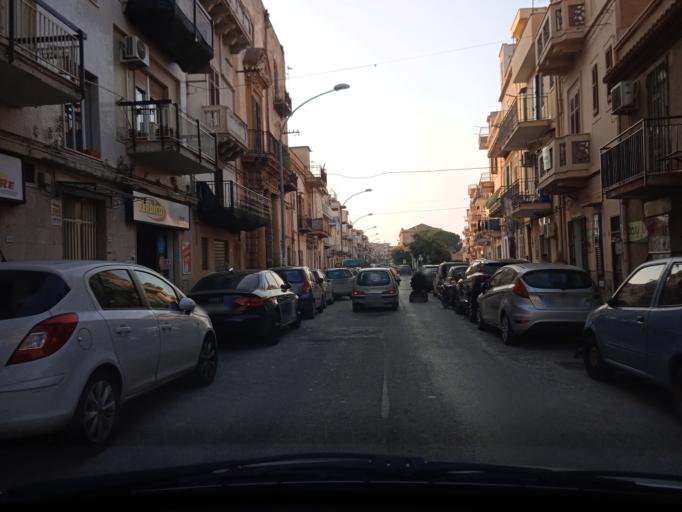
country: IT
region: Sicily
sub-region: Palermo
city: Villabate
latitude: 38.0782
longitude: 13.4410
